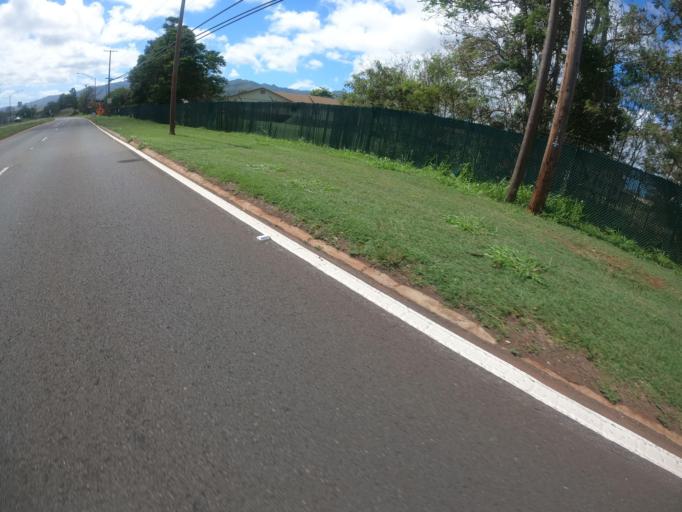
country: US
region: Hawaii
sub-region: Honolulu County
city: Schofield Barracks
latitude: 21.4816
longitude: -158.0485
